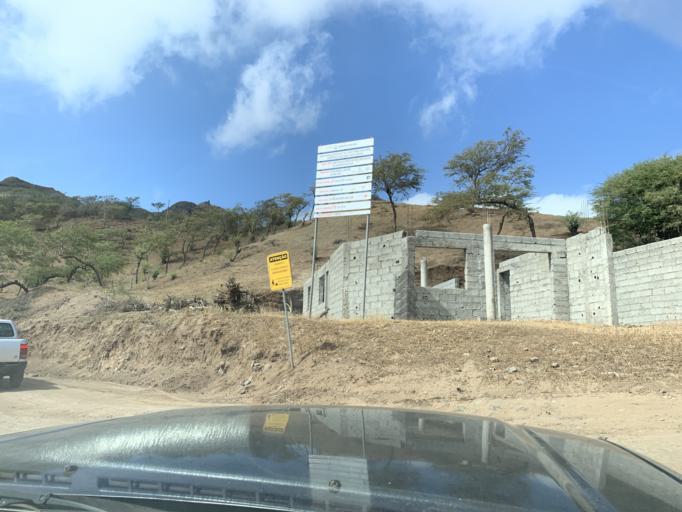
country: CV
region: Praia
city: Praia
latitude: 14.9124
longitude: -23.5281
